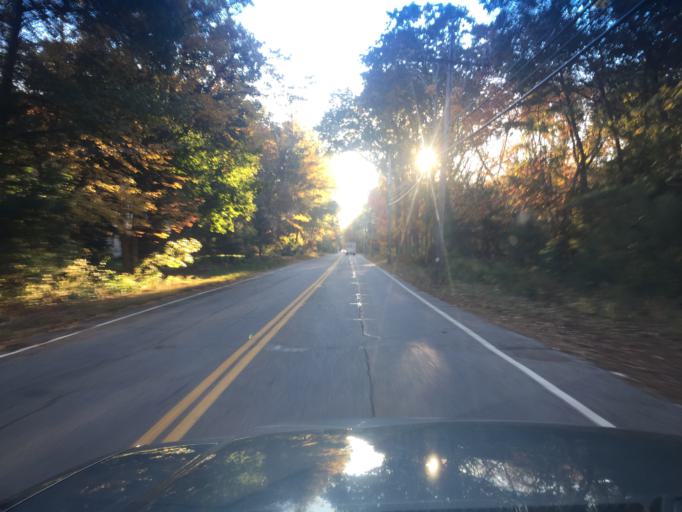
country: US
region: Massachusetts
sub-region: Middlesex County
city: Hudson
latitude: 42.3968
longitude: -71.5333
